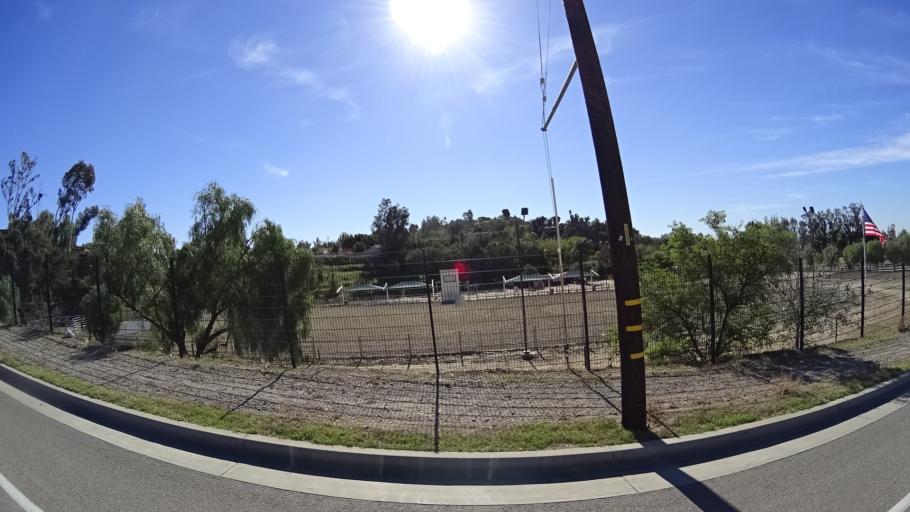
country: US
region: California
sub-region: Orange County
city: Villa Park
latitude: 33.8135
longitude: -117.7857
